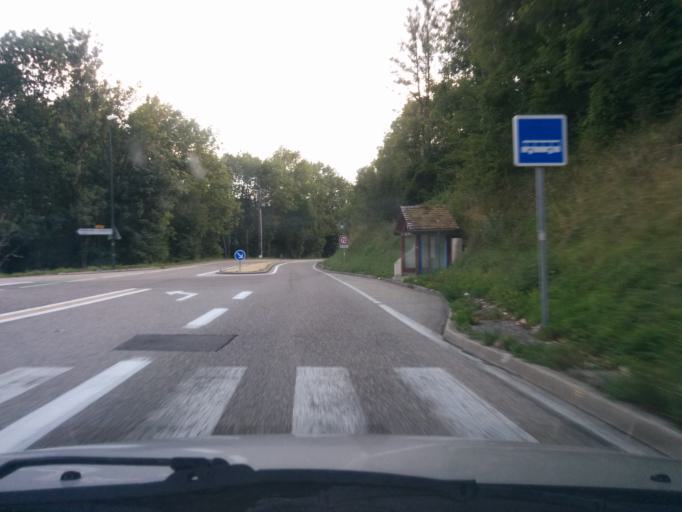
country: FR
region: Rhone-Alpes
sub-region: Departement de l'Isere
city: Voreppe
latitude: 45.3190
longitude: 5.6530
